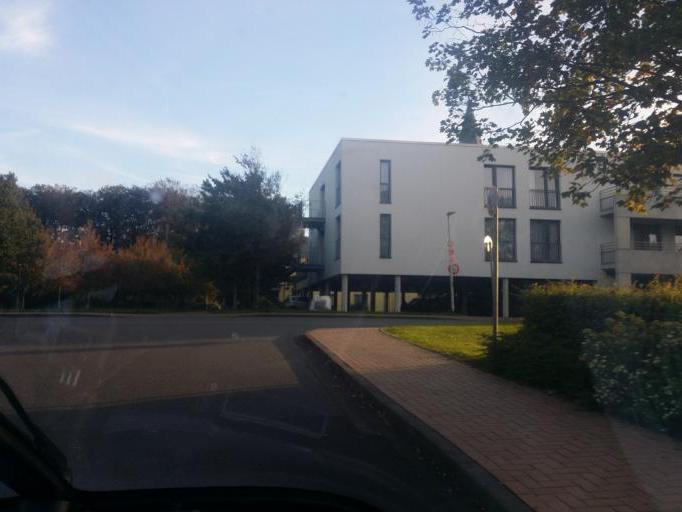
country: DE
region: Schleswig-Holstein
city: Husum
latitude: 54.4833
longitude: 9.0474
